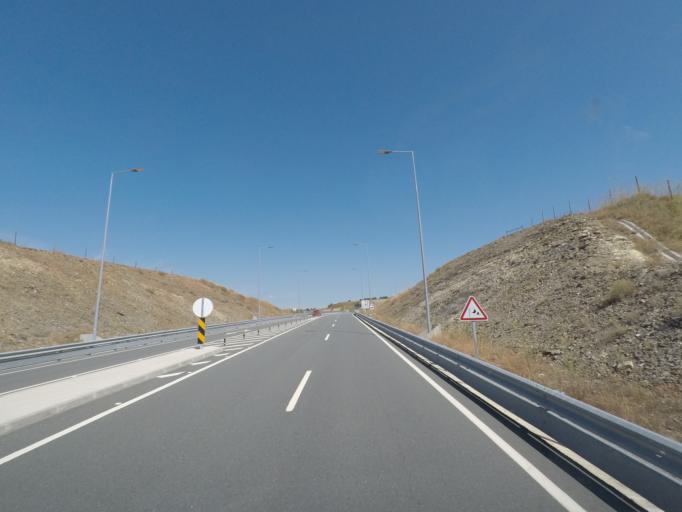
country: PT
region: Braganca
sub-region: Alfandega da Fe
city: Alfandega da Fe
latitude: 41.2818
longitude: -6.8936
